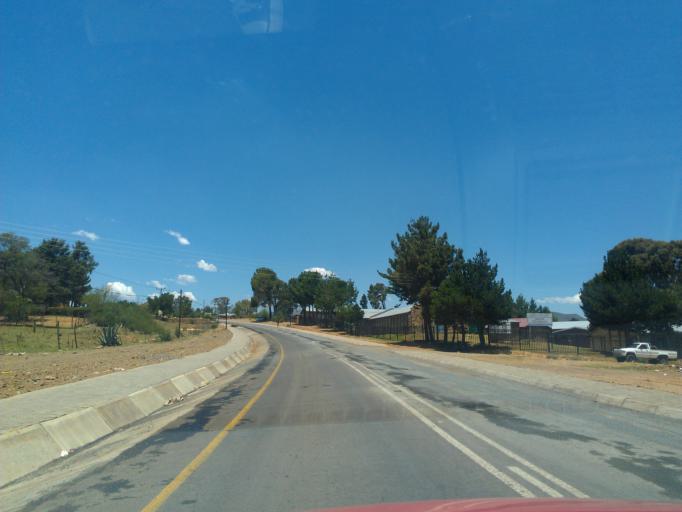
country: LS
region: Berea
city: Teyateyaneng
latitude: -29.1128
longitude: 27.9675
